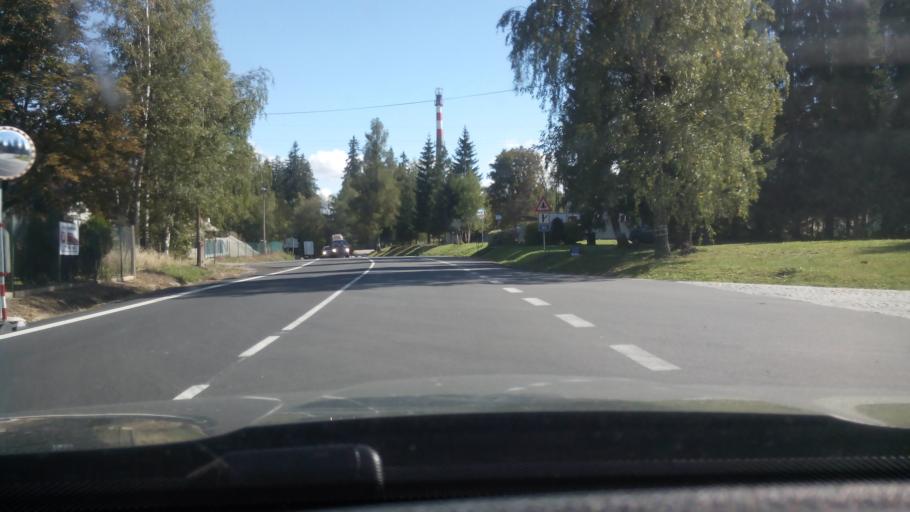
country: CZ
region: Jihocesky
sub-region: Okres Prachatice
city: Zdikov
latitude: 49.0631
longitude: 13.7374
